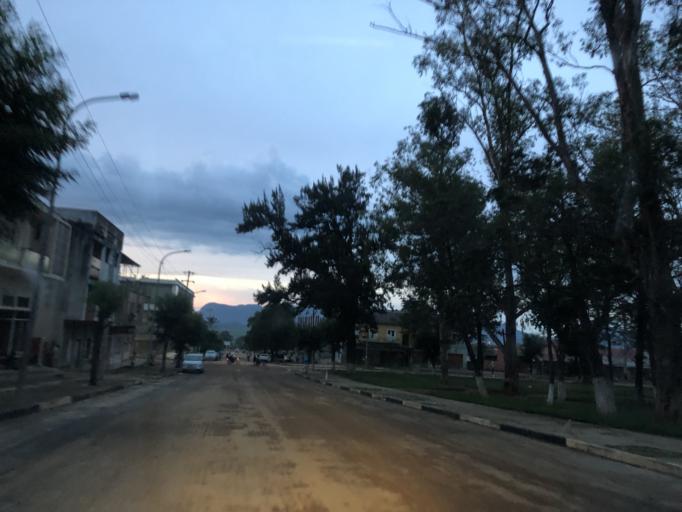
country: AO
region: Cuanza Sul
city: Uacu Cungo
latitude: -11.3651
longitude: 15.1174
